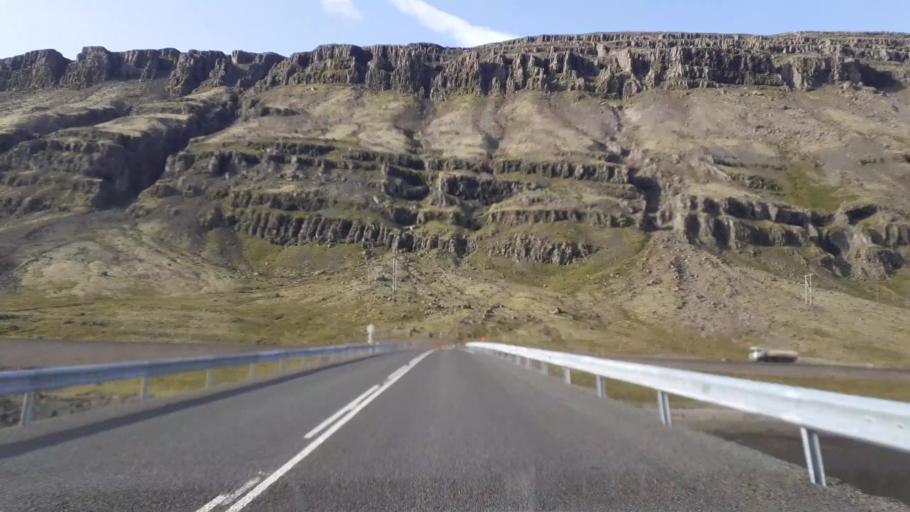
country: IS
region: East
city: Reydarfjoerdur
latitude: 64.7868
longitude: -14.4914
